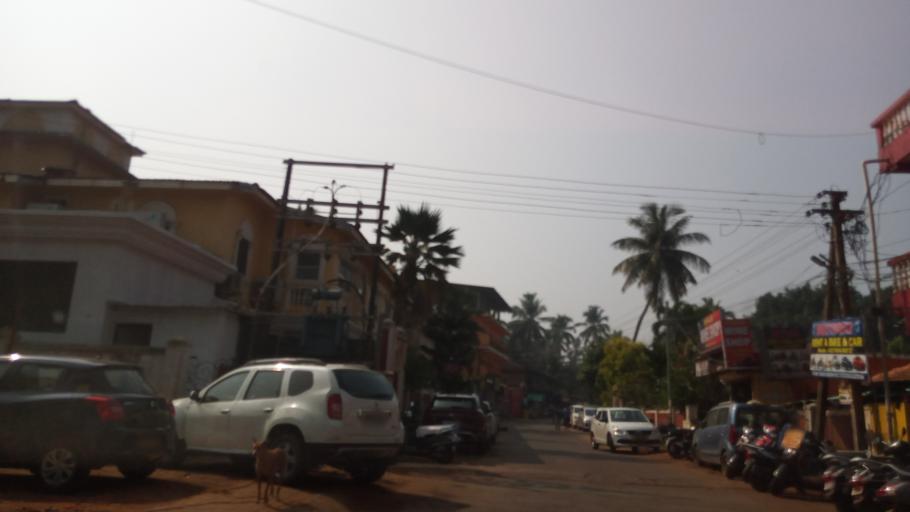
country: IN
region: Goa
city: Calangute
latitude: 15.5410
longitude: 73.7609
